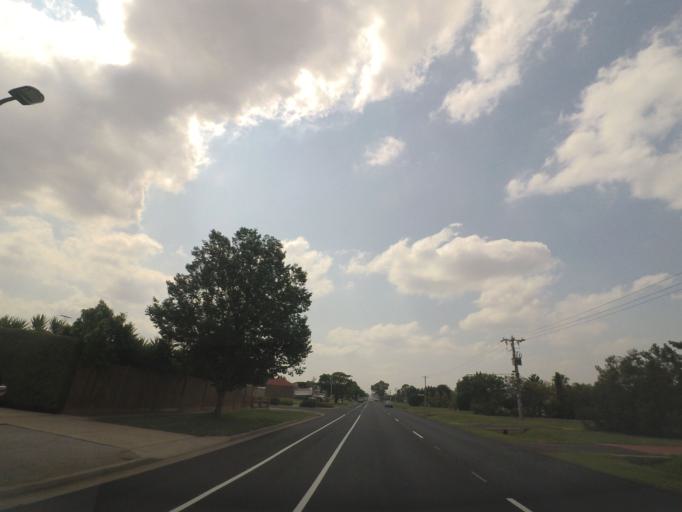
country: AU
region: Victoria
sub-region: Melton
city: Brookfield
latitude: -37.7005
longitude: 144.5545
